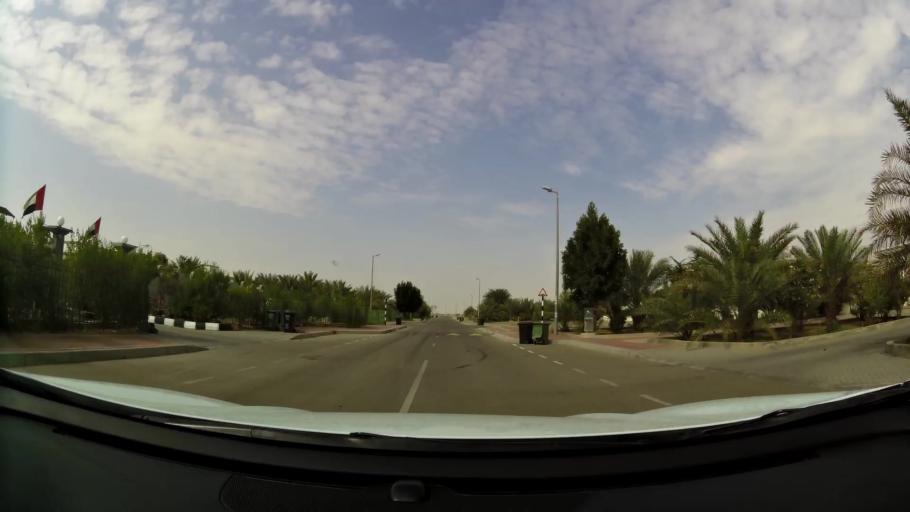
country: AE
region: Abu Dhabi
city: Al Ain
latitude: 24.0996
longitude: 55.8973
